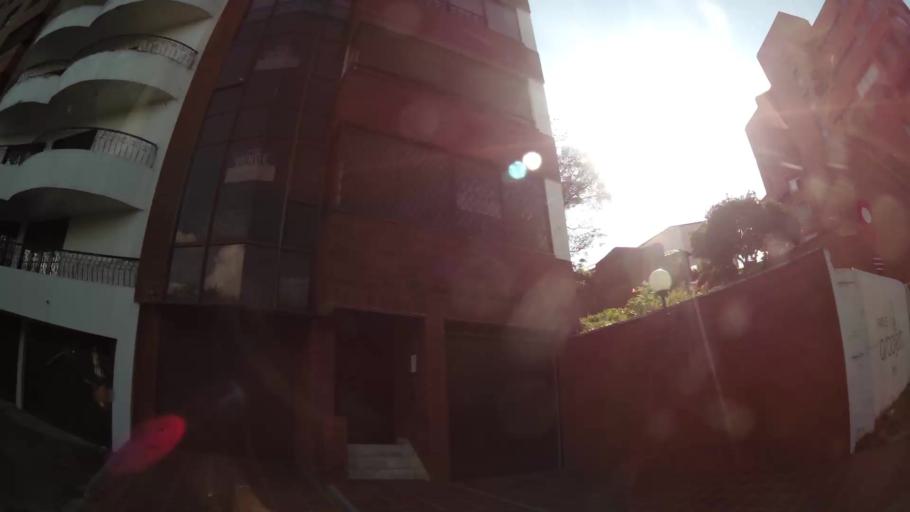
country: CO
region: Valle del Cauca
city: Cali
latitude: 3.4474
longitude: -76.5477
